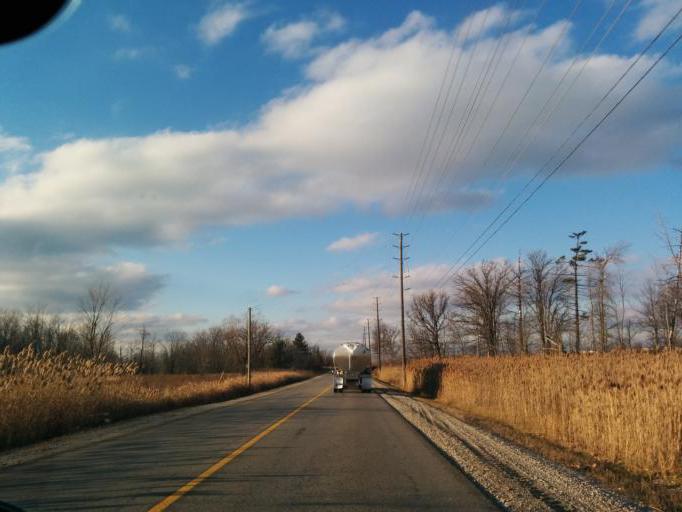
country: CA
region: Ontario
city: Oakville
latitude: 43.5169
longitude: -79.7090
